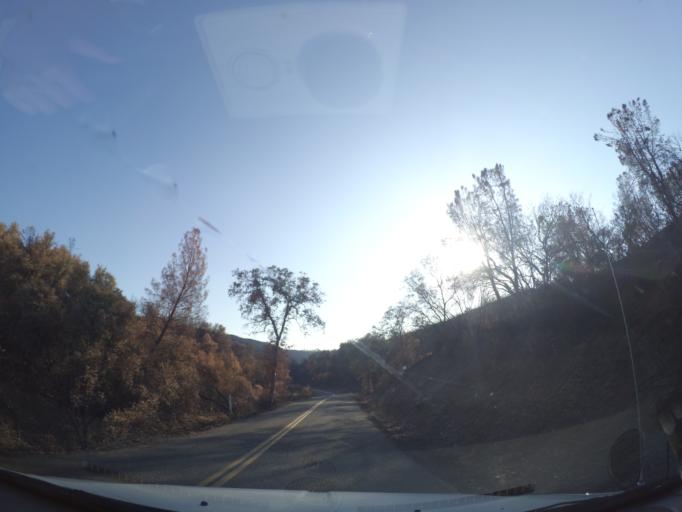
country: US
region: California
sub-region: Mariposa County
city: Mariposa
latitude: 37.5079
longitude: -120.0605
